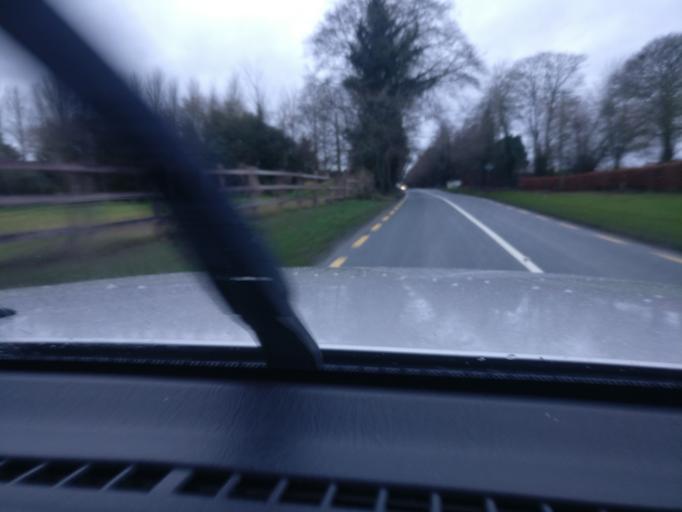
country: IE
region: Leinster
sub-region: An Mhi
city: Trim
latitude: 53.5209
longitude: -6.8250
